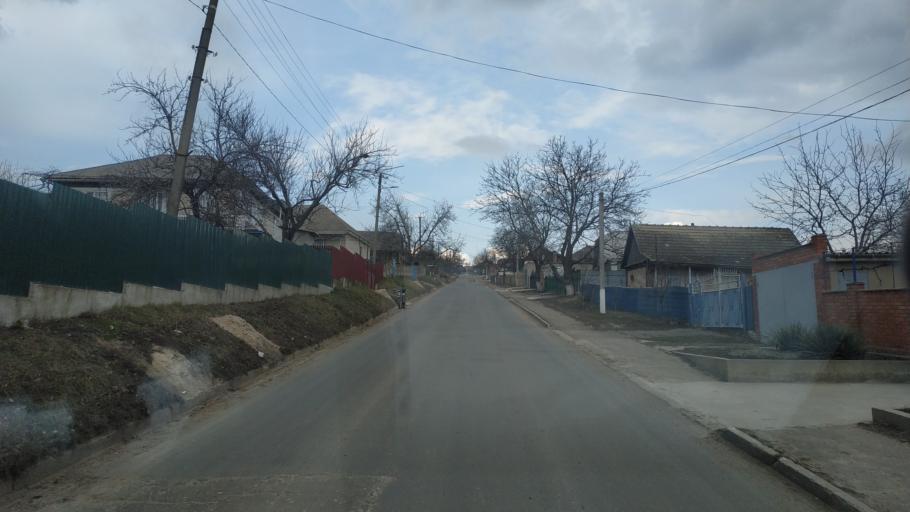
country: MD
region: Anenii Noi
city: Varnita
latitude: 46.8454
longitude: 29.3572
